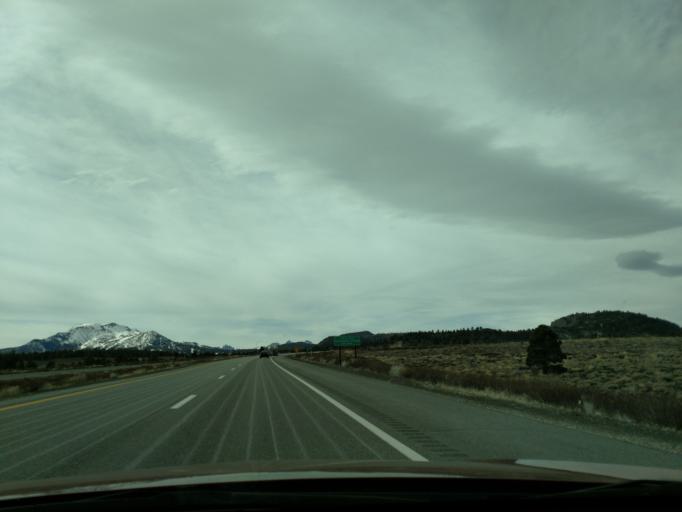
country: US
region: California
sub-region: Mono County
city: Mammoth Lakes
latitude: 37.6388
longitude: -118.9089
